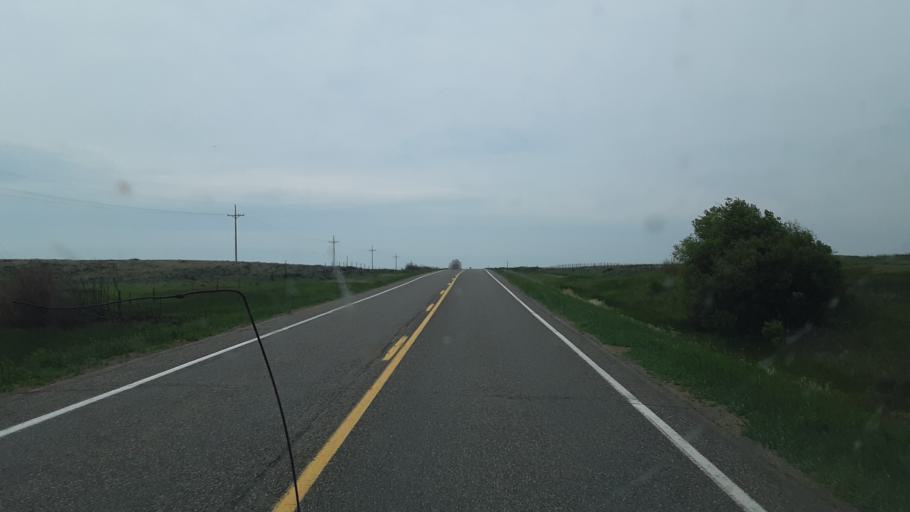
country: US
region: Colorado
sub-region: Jackson County
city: Walden
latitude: 40.8504
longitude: -106.3090
